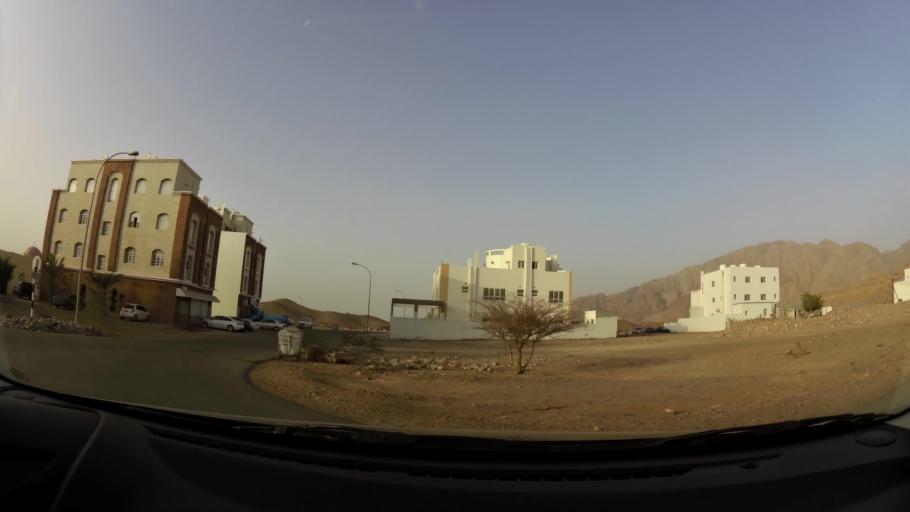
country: OM
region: Muhafazat Masqat
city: Bawshar
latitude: 23.5093
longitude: 58.3462
